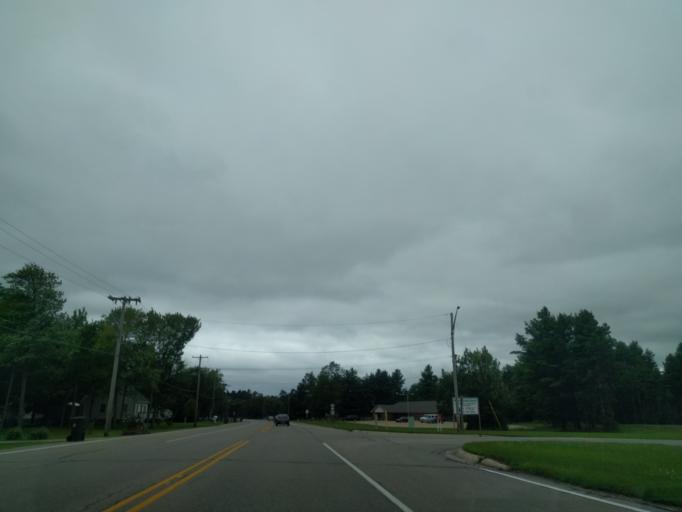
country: US
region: Michigan
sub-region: Delta County
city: Escanaba
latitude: 45.7137
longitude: -87.0873
